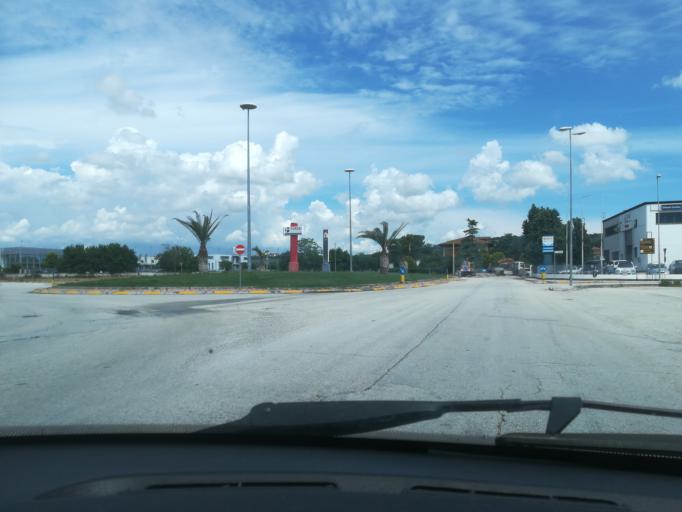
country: IT
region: The Marches
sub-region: Provincia di Macerata
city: Santa Maria Apparente
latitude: 43.2870
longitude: 13.6816
